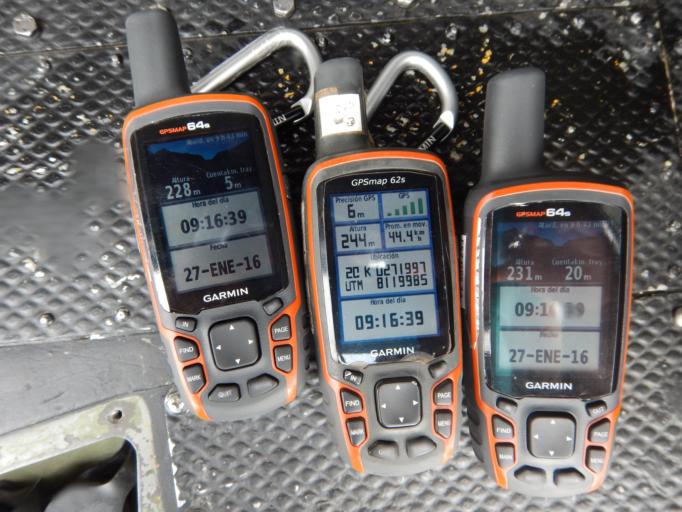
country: BO
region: Cochabamba
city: Chimore
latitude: -16.9929
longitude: -65.1416
